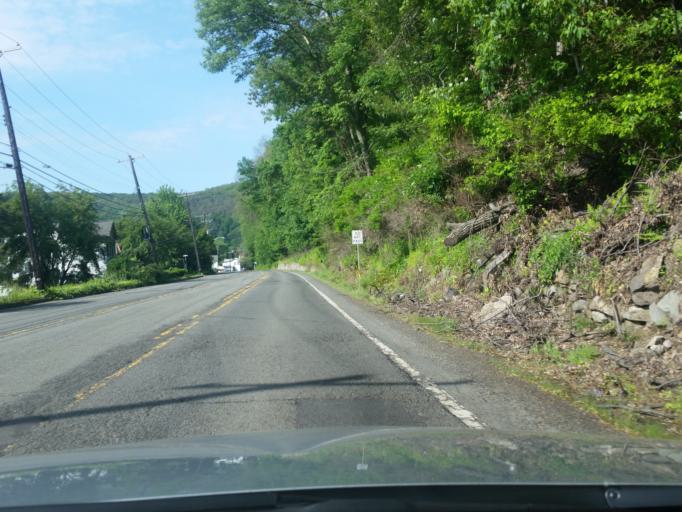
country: US
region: Pennsylvania
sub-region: Luzerne County
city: Glen Lyon
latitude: 41.1580
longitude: -76.1460
